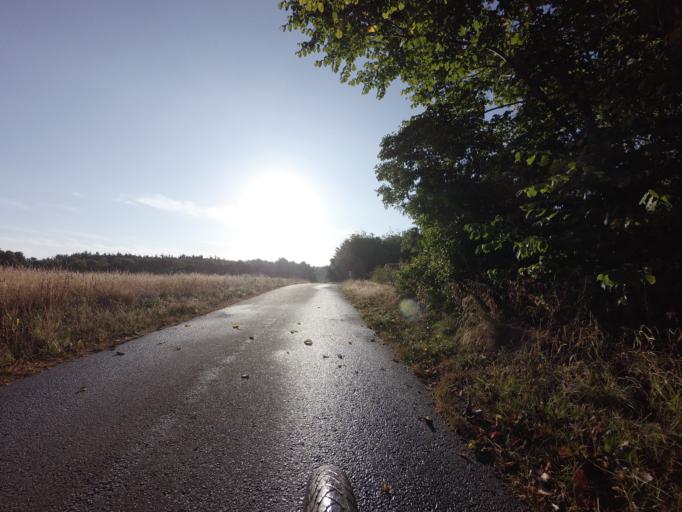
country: DK
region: North Denmark
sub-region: Hjorring Kommune
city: Vra
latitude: 57.3629
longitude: 9.8695
